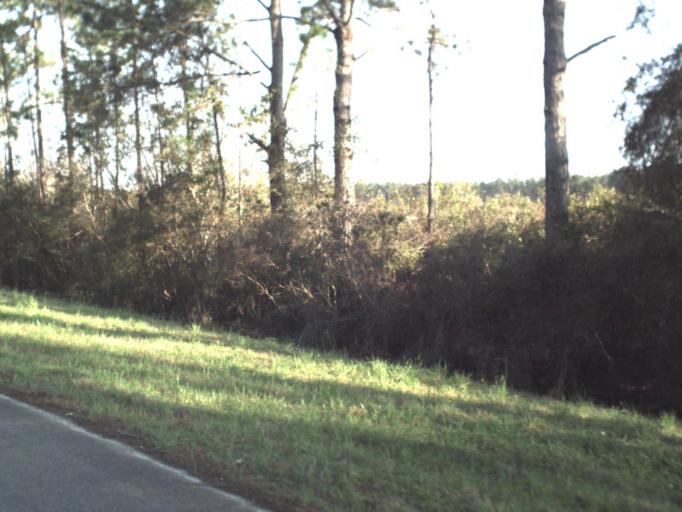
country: US
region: Florida
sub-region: Bay County
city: Lynn Haven
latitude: 30.4393
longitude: -85.7413
